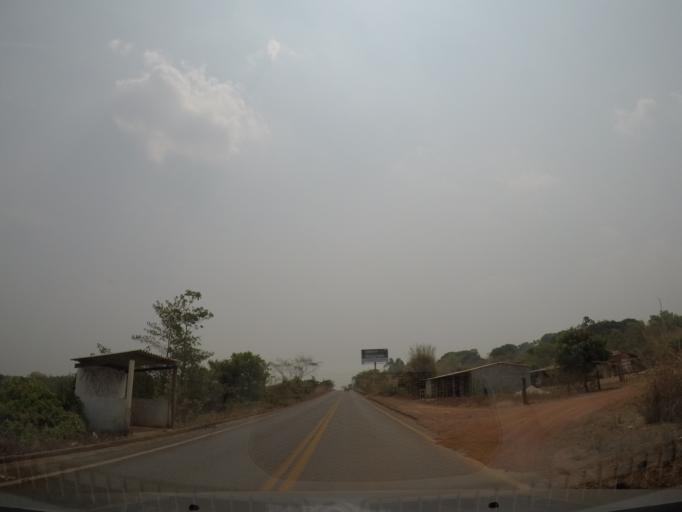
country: BR
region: Goias
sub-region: Pirenopolis
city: Pirenopolis
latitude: -15.9011
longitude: -48.8681
